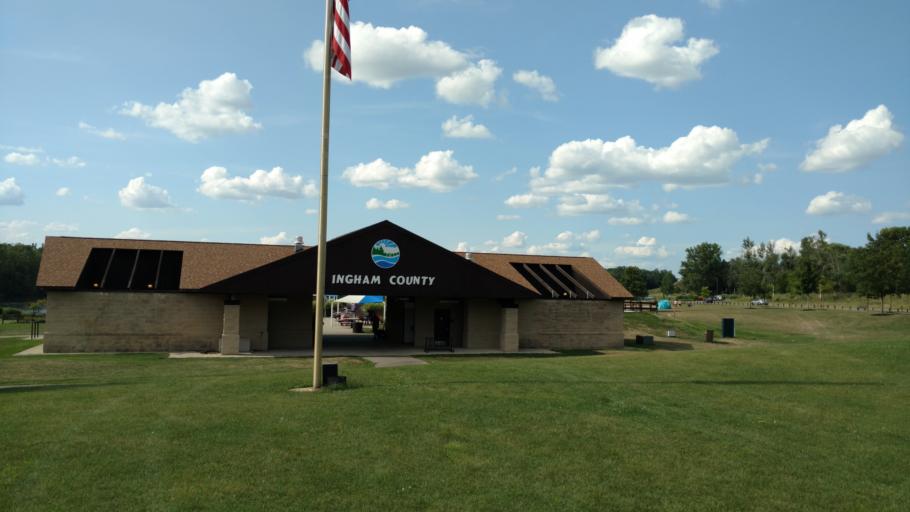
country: US
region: Michigan
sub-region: Ingham County
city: Lansing
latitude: 42.6918
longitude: -84.5294
